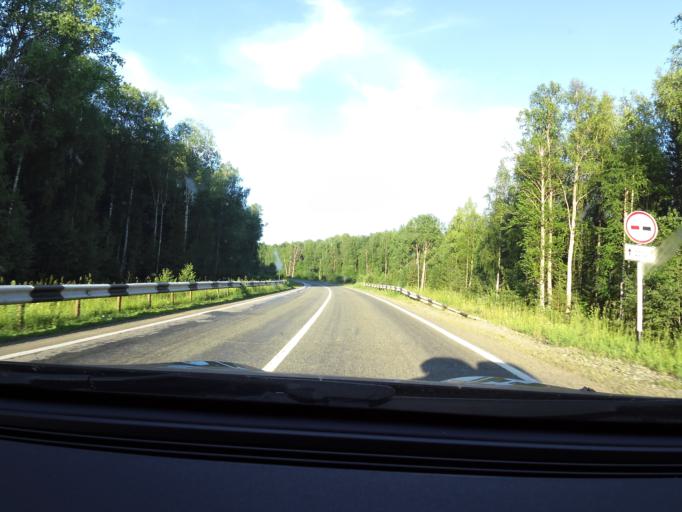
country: RU
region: Kirov
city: Kostino
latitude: 58.6402
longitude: 53.8074
